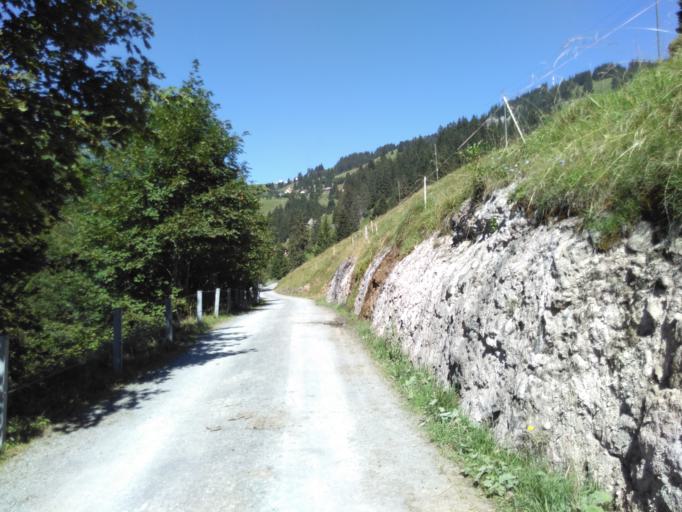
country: CH
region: Lucerne
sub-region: Lucerne-Land District
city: Vitznau
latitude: 47.0403
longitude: 8.4924
